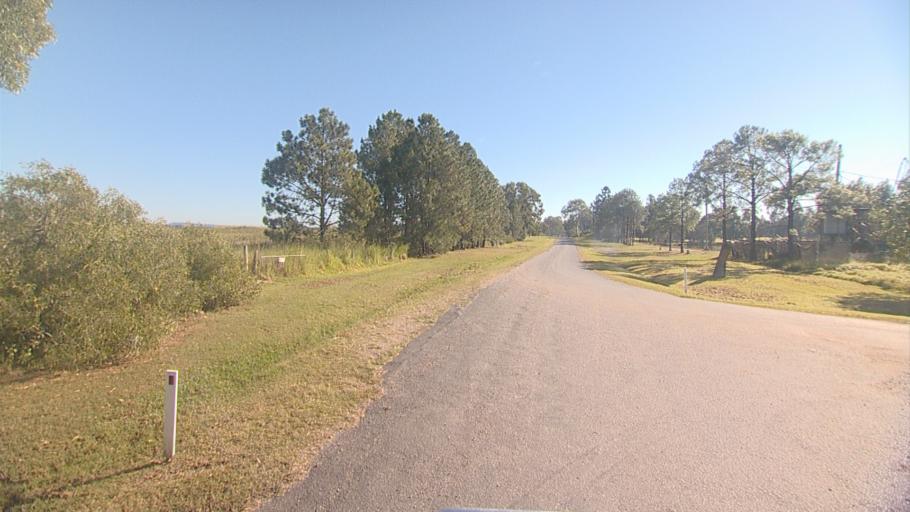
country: AU
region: Queensland
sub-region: Gold Coast
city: Yatala
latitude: -27.6914
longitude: 153.2607
